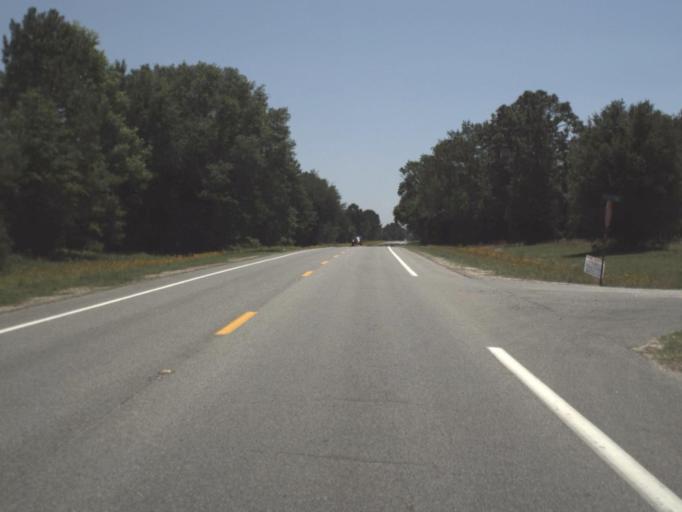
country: US
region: Florida
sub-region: Suwannee County
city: Live Oak
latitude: 30.3708
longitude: -83.1507
